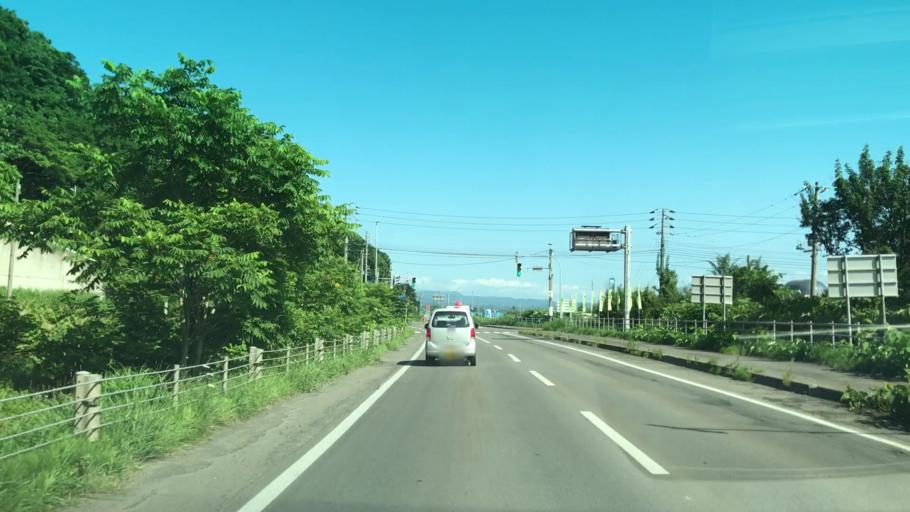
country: JP
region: Hokkaido
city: Iwanai
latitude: 43.0346
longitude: 140.5285
